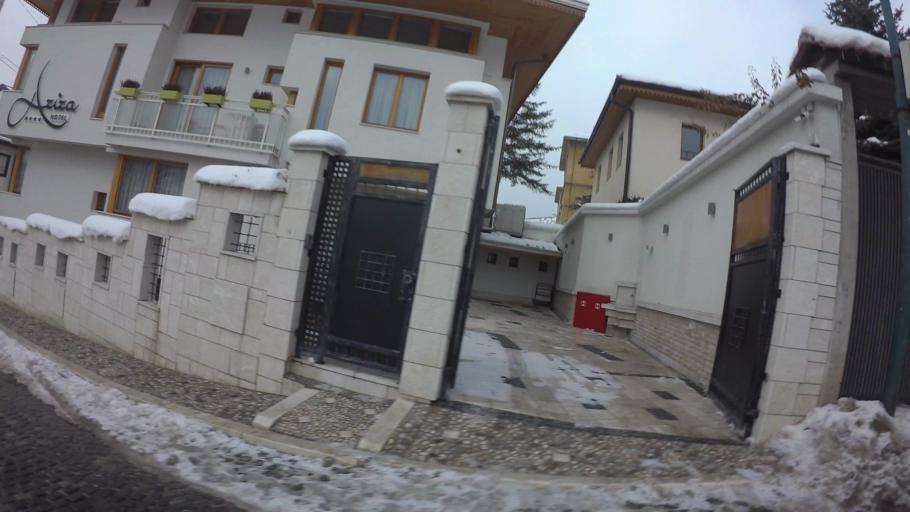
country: BA
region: Federation of Bosnia and Herzegovina
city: Kobilja Glava
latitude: 43.8633
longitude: 18.4364
